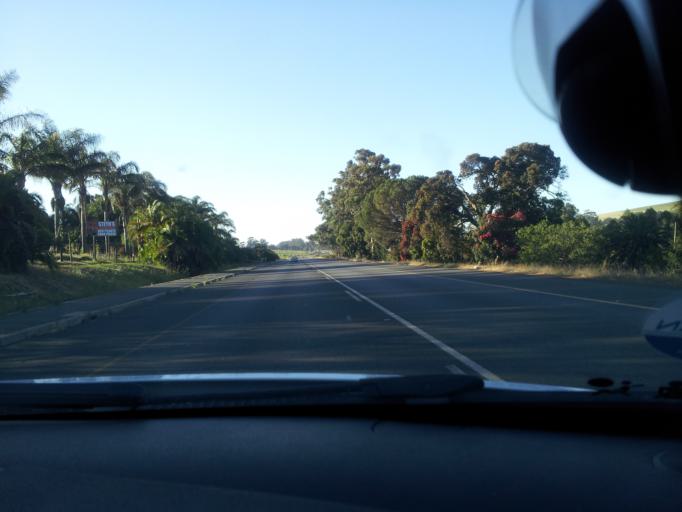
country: ZA
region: Western Cape
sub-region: Cape Winelands District Municipality
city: Stellenbosch
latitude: -33.9068
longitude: 18.8447
